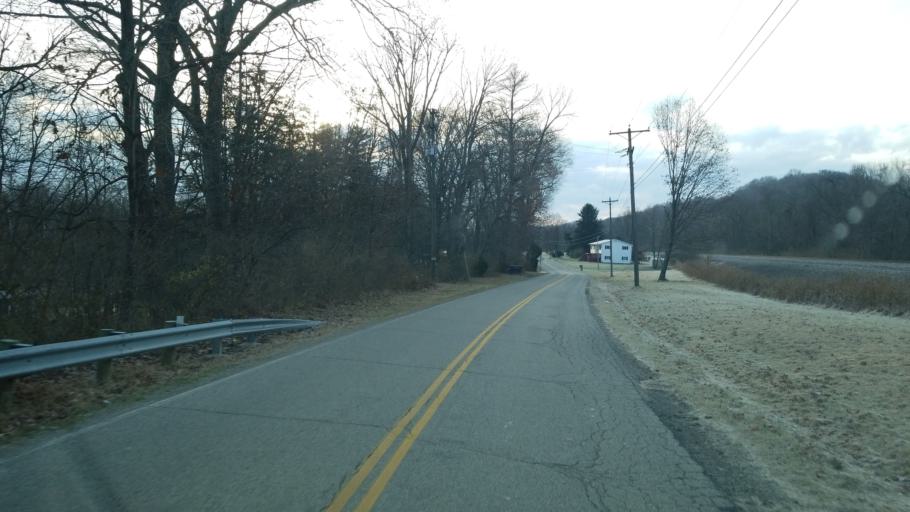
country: US
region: Ohio
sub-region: Ross County
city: Chillicothe
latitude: 39.2724
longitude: -82.9271
